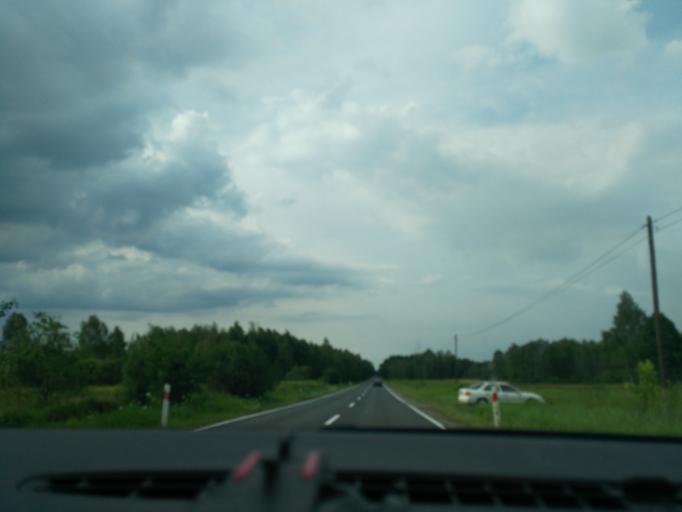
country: PL
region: Subcarpathian Voivodeship
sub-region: Powiat nizanski
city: Jezowe
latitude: 50.3908
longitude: 22.1298
